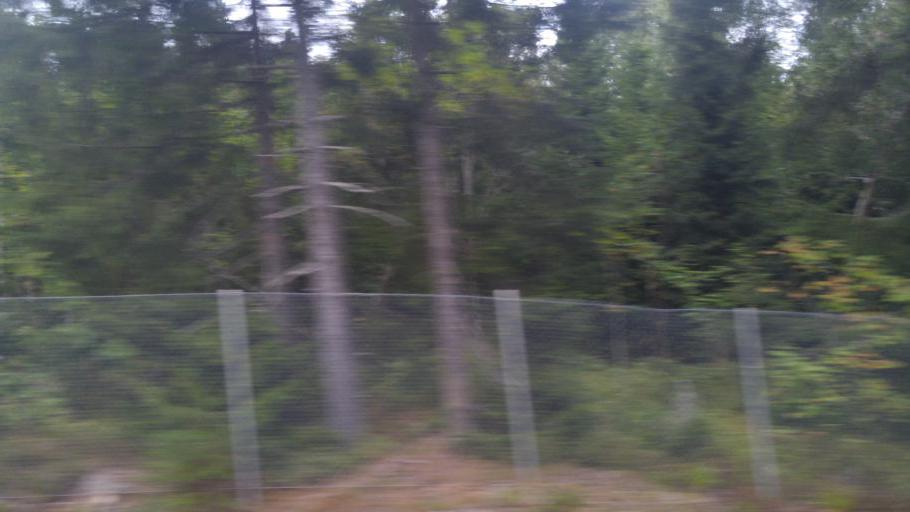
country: NO
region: Oslo
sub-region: Oslo
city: Sjolyststranda
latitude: 59.9611
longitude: 10.6855
